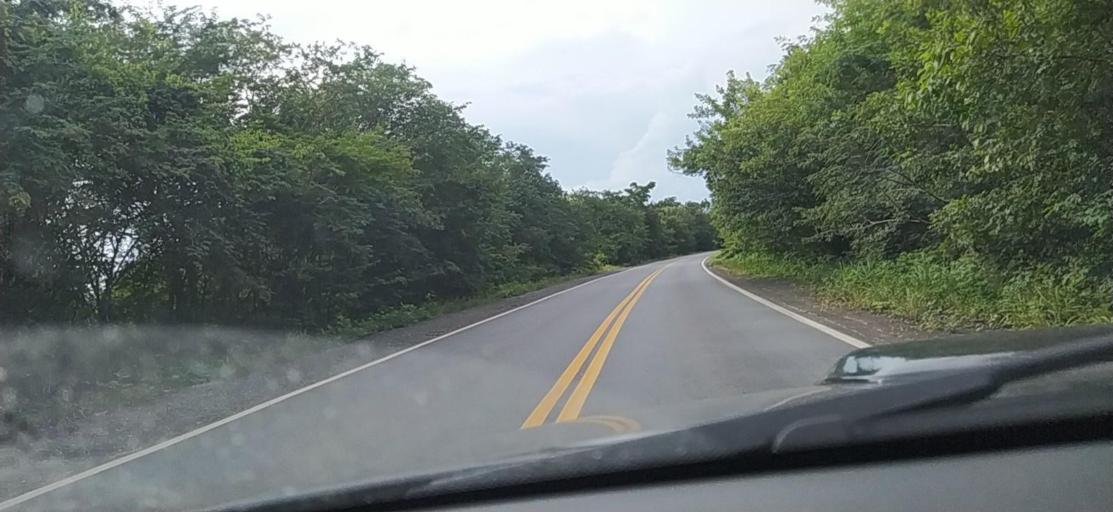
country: BR
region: Minas Gerais
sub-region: Francisco Sa
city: Francisco Sa
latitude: -16.5282
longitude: -43.6793
